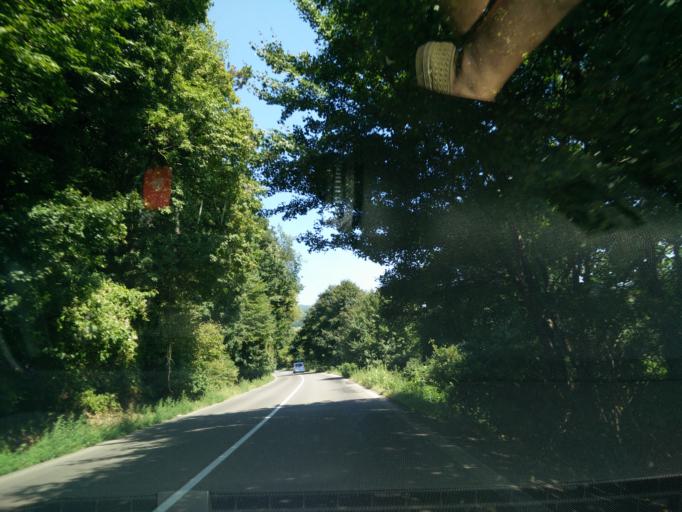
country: SK
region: Banskobystricky
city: Nova Bana
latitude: 48.4026
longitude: 18.6209
